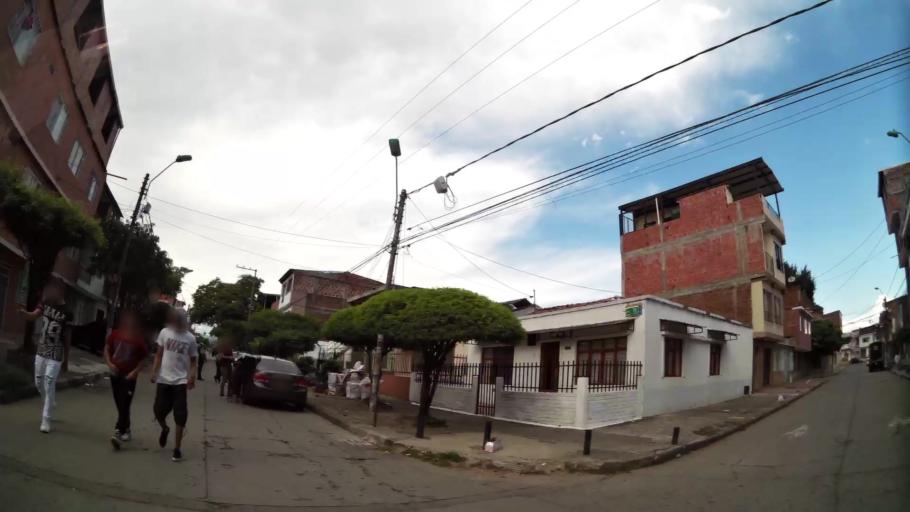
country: CO
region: Valle del Cauca
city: Cali
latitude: 3.4236
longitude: -76.5226
